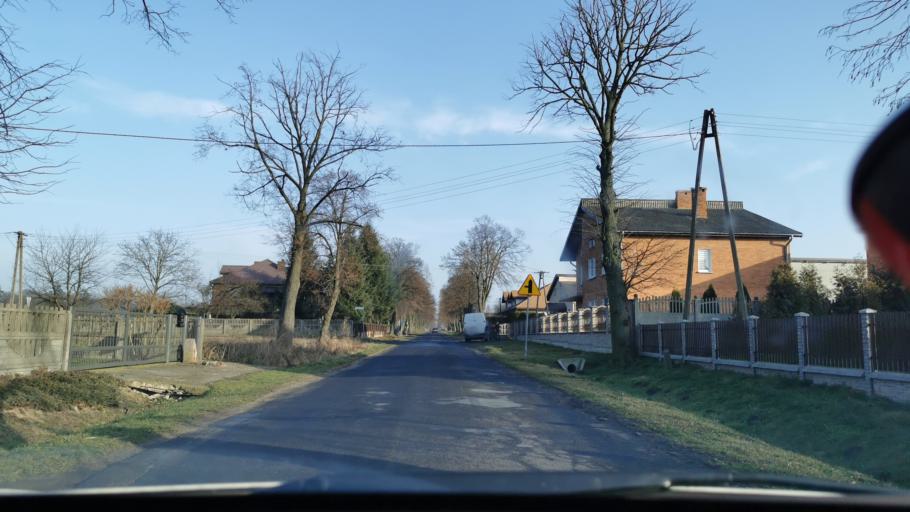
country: PL
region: Greater Poland Voivodeship
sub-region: Powiat kaliski
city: Kozminek
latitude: 51.6851
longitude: 18.3206
